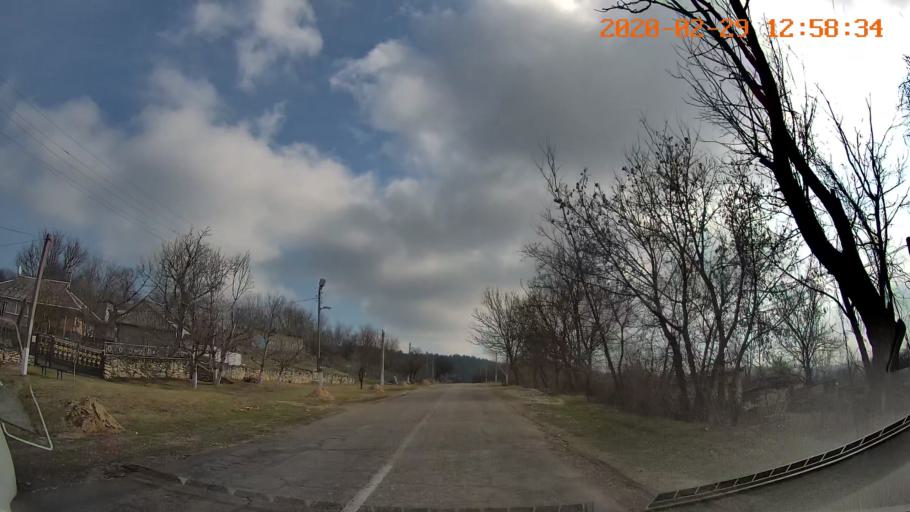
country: MD
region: Telenesti
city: Camenca
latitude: 48.0695
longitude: 28.7220
